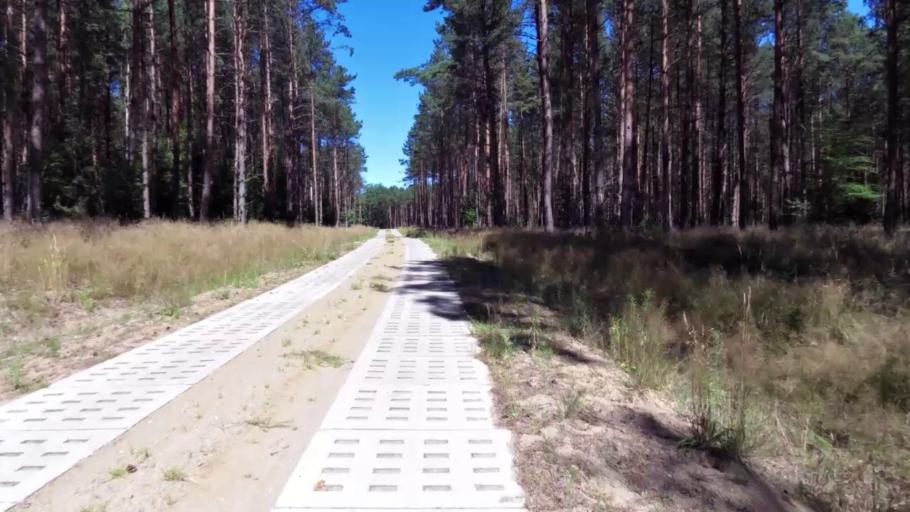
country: PL
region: West Pomeranian Voivodeship
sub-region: Powiat szczecinecki
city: Szczecinek
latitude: 53.6111
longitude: 16.6648
